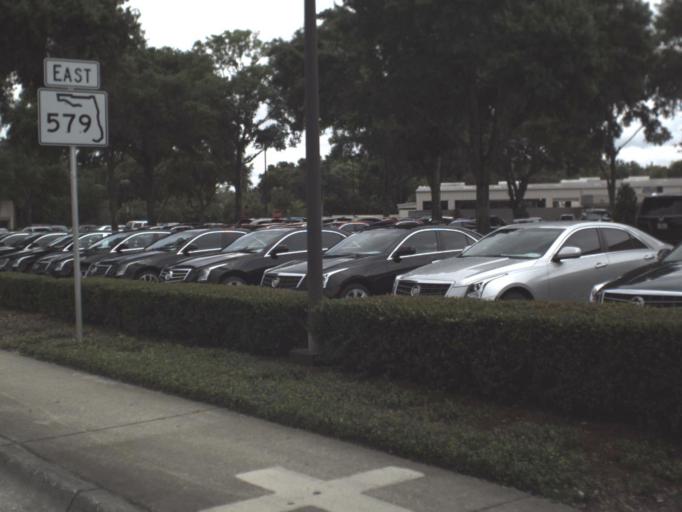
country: US
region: Florida
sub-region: Hillsborough County
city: Lake Magdalene
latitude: 28.0692
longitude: -82.4587
